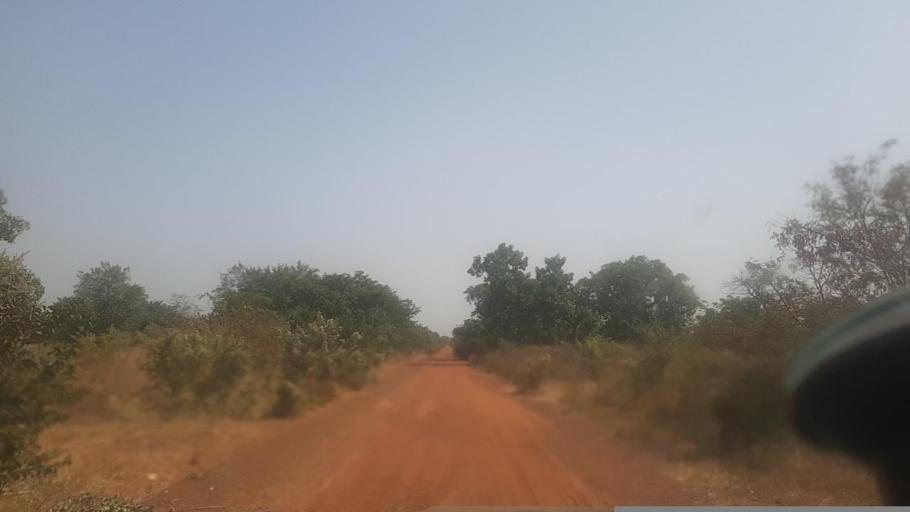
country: ML
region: Segou
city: Bla
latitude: 12.9242
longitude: -6.2676
